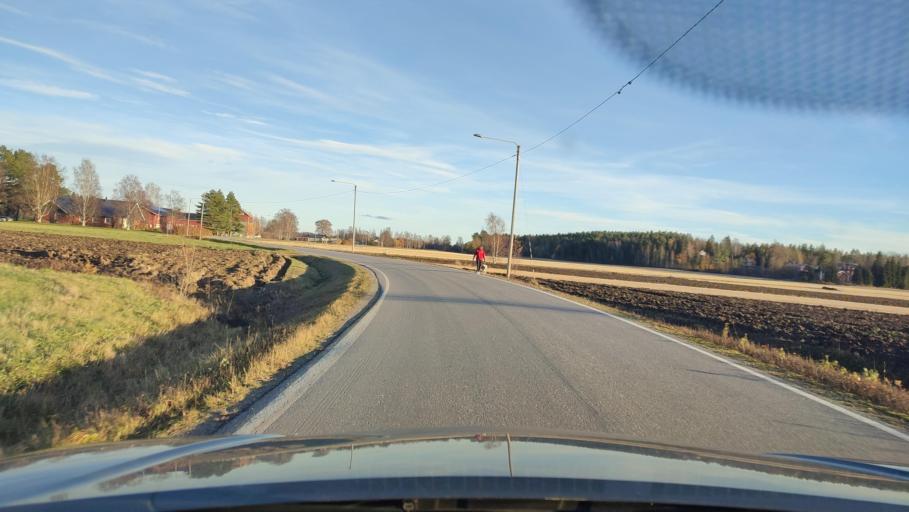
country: FI
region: Ostrobothnia
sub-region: Vaasa
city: Ristinummi
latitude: 62.9985
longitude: 21.7043
